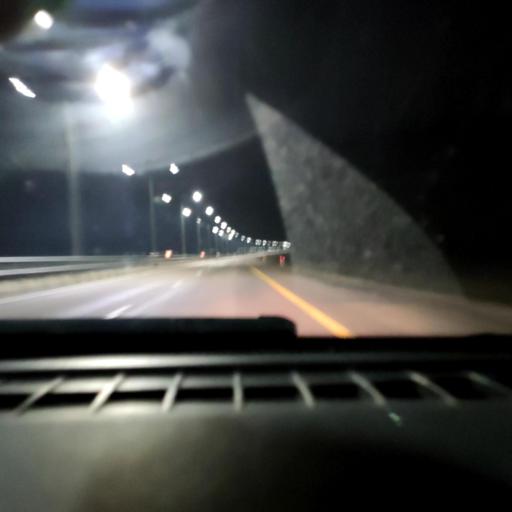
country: RU
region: Voronezj
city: Podkletnoye
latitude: 51.5150
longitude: 39.5119
